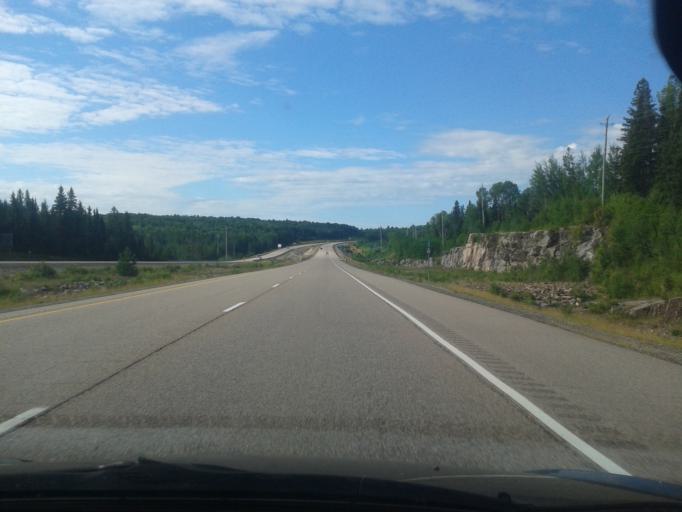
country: CA
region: Ontario
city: South River
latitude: 45.9189
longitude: -79.3653
